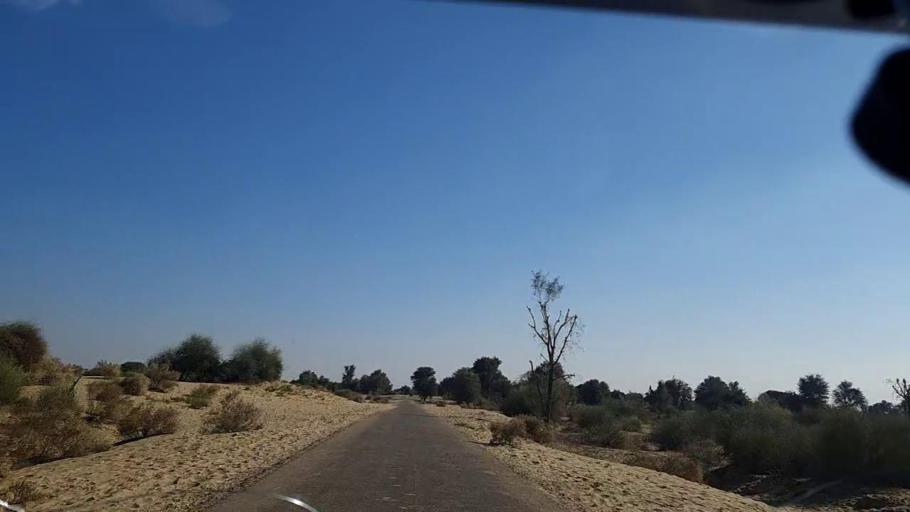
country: PK
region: Sindh
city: Khanpur
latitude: 27.6178
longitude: 69.4444
